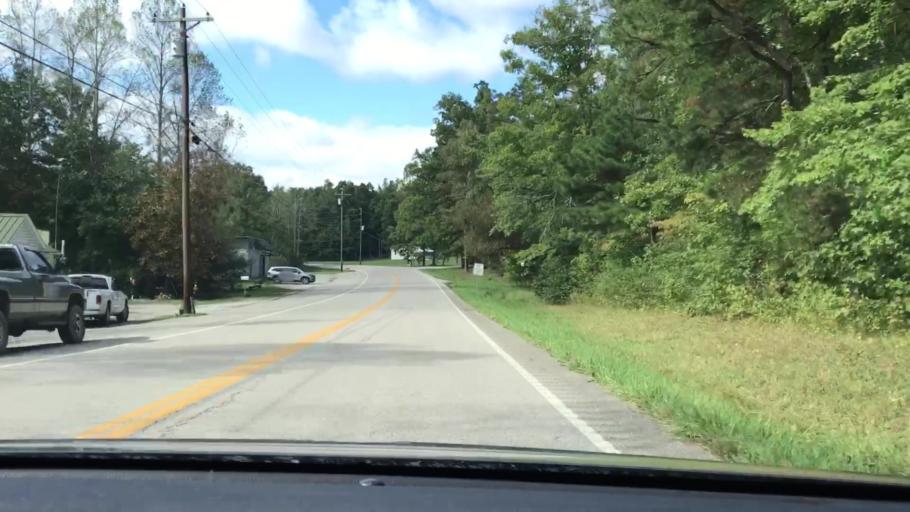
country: US
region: Tennessee
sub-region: Scott County
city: Huntsville
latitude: 36.3369
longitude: -84.6104
